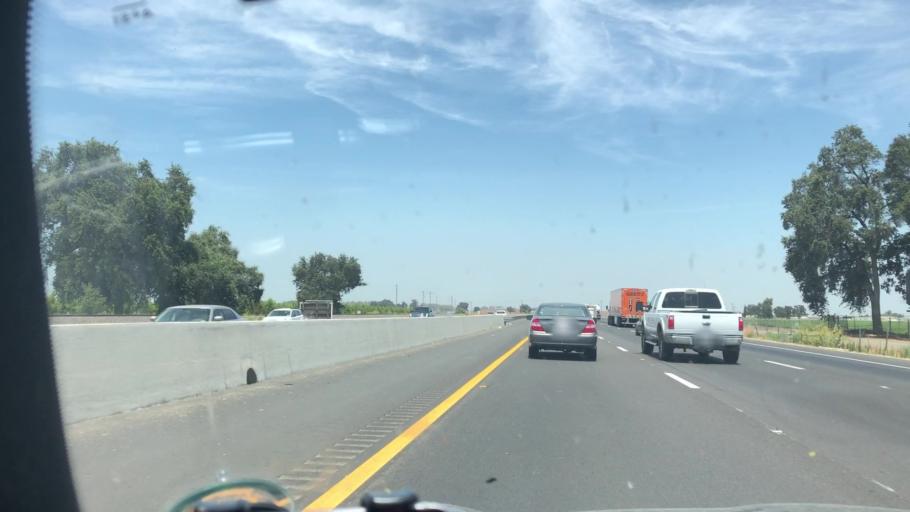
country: US
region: California
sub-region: Tulare County
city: Goshen
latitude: 36.3071
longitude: -119.3910
